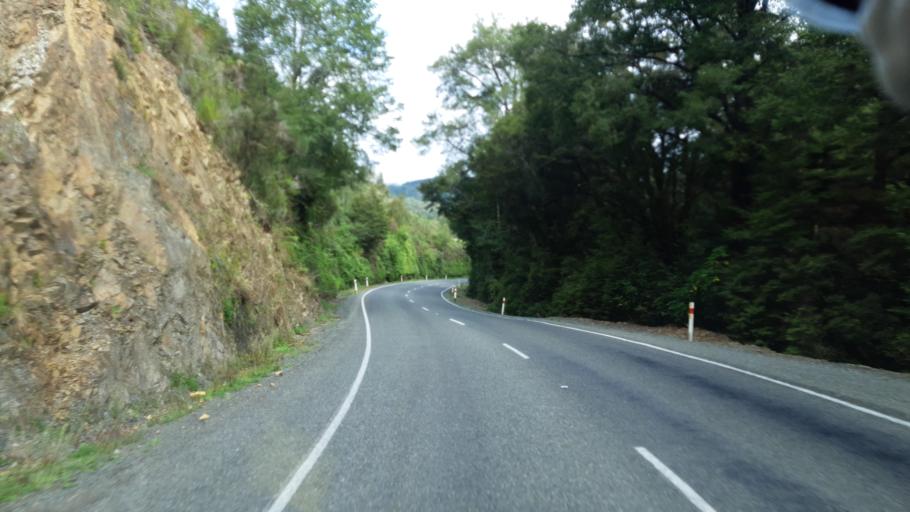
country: NZ
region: West Coast
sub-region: Buller District
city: Westport
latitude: -41.9851
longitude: 172.2080
